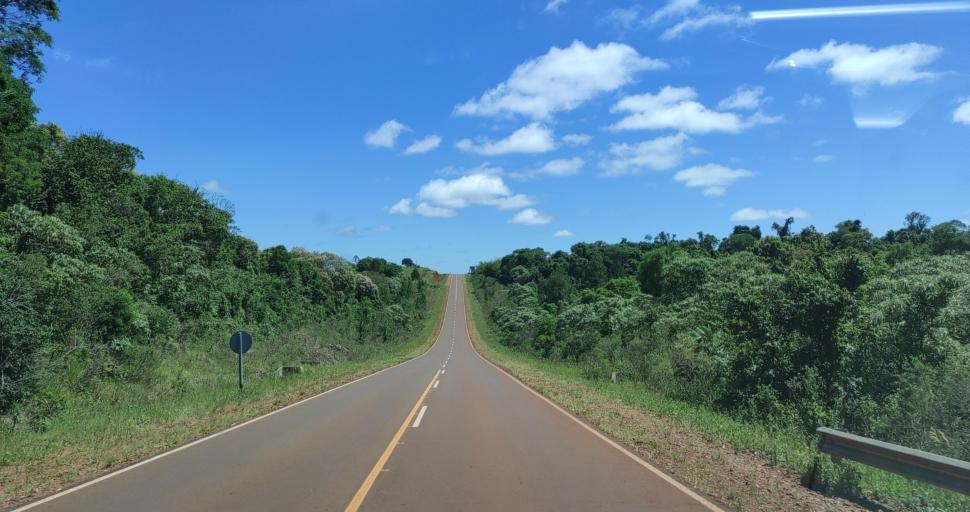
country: AR
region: Misiones
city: Campo Grande
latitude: -27.3168
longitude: -54.8984
